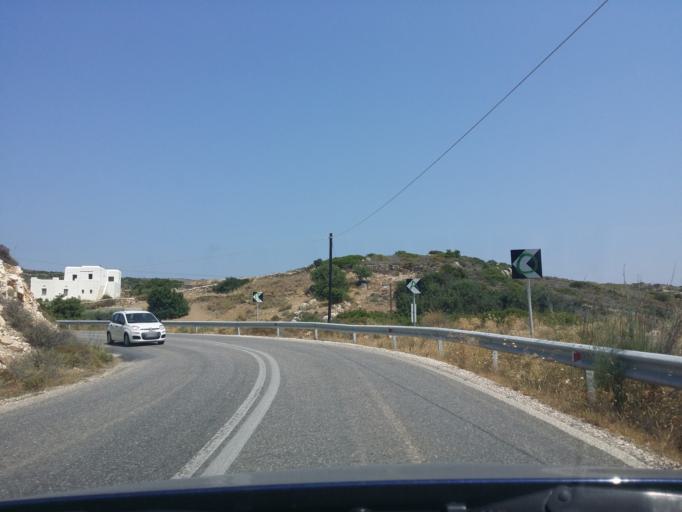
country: GR
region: South Aegean
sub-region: Nomos Kykladon
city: Naousa
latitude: 37.0596
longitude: 25.2366
